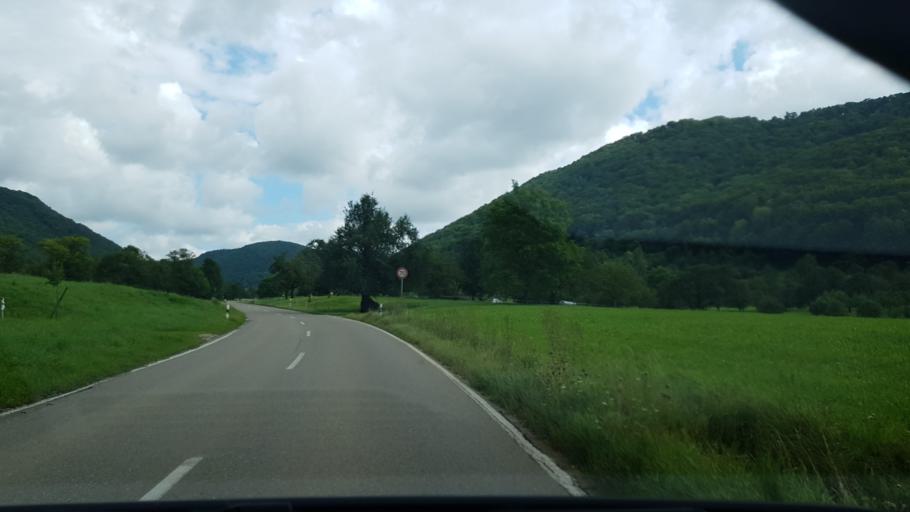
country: DE
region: Baden-Wuerttemberg
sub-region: Tuebingen Region
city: Grabenstetten
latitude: 48.5431
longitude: 9.4795
